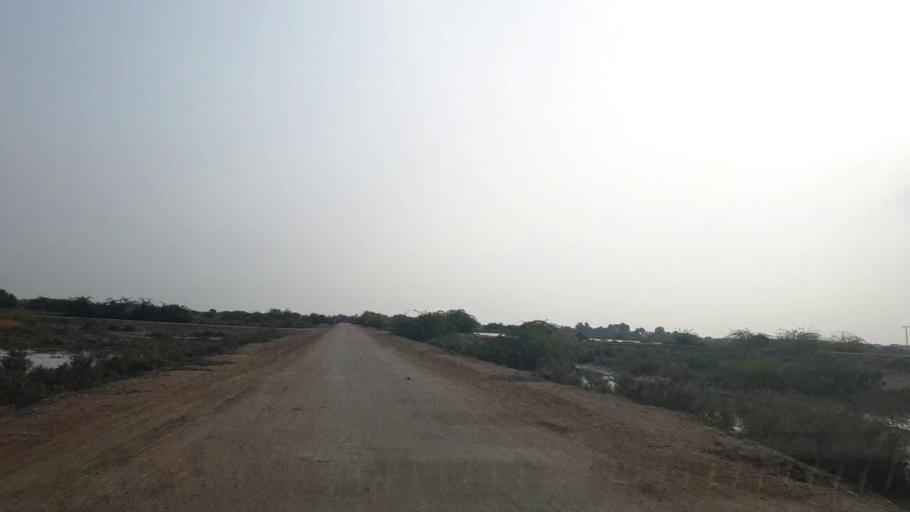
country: PK
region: Sindh
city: Badin
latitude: 24.6311
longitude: 68.6923
